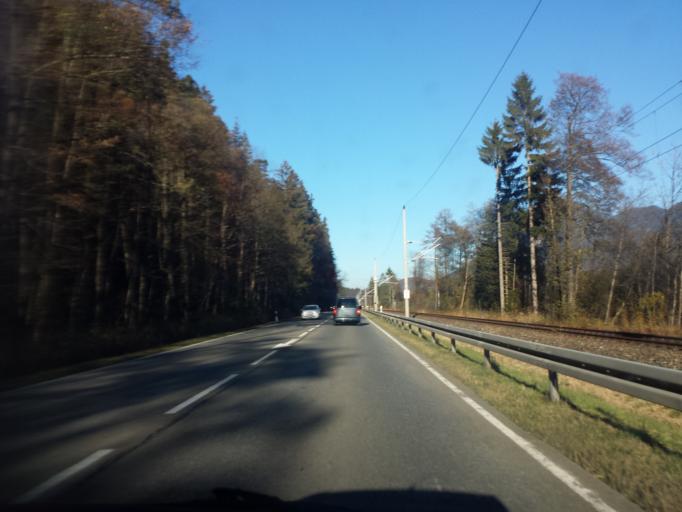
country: DE
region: Bavaria
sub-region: Upper Bavaria
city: Eschenlohe
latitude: 47.5778
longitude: 11.1647
